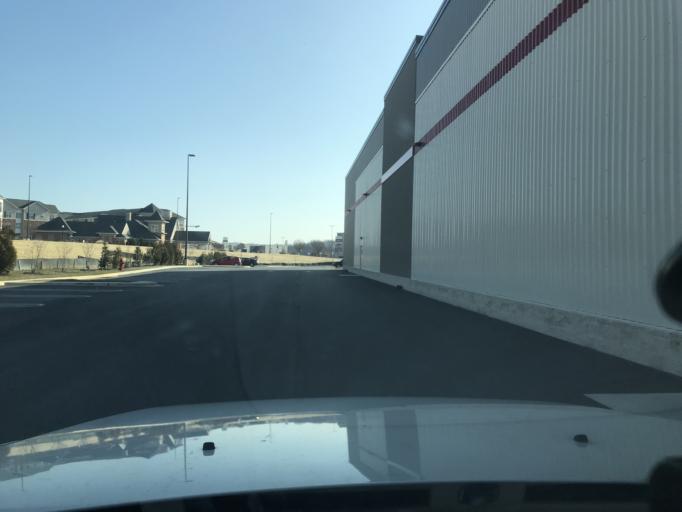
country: US
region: Maryland
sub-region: Baltimore County
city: Owings Mills
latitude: 39.4075
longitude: -76.7891
